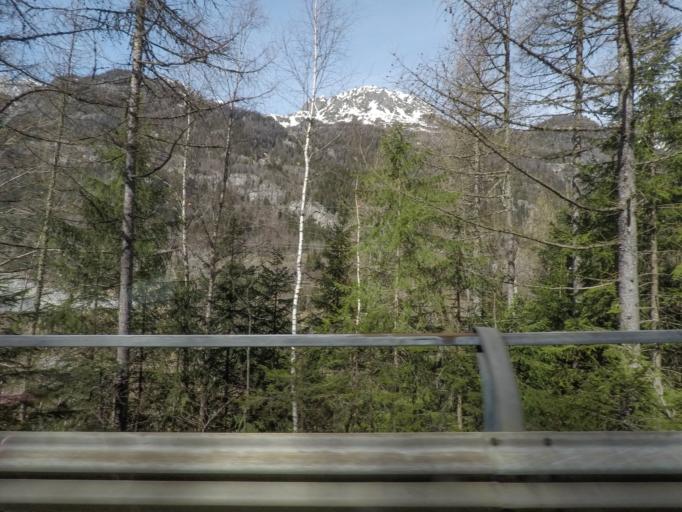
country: CH
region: Valais
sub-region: Saint-Maurice District
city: Salvan
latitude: 46.0656
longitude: 6.9669
